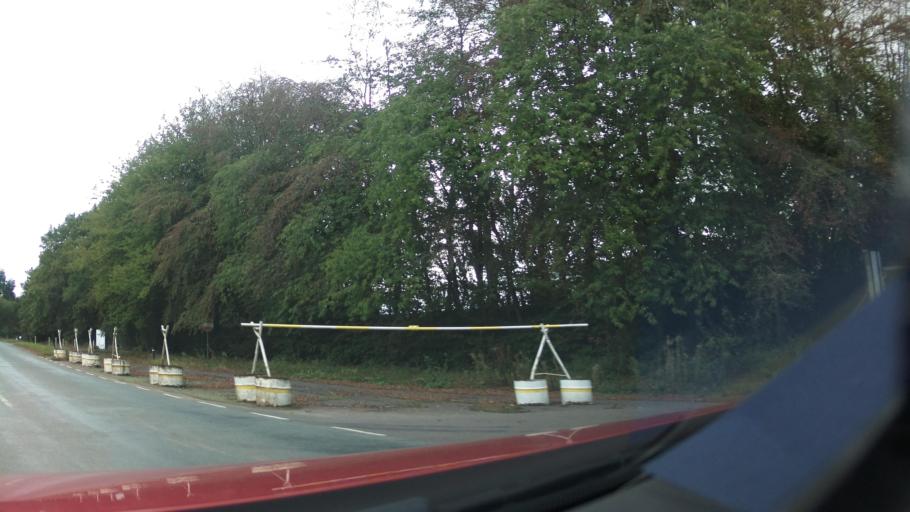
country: GB
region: England
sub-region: Staffordshire
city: Eccleshall
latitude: 52.8950
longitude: -2.2155
